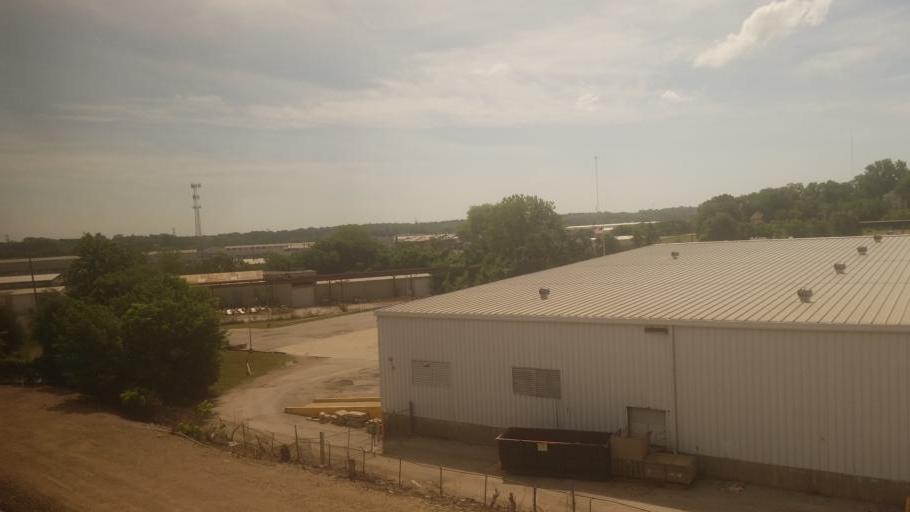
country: US
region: Missouri
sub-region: Clay County
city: North Kansas City
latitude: 39.1082
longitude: -94.5068
